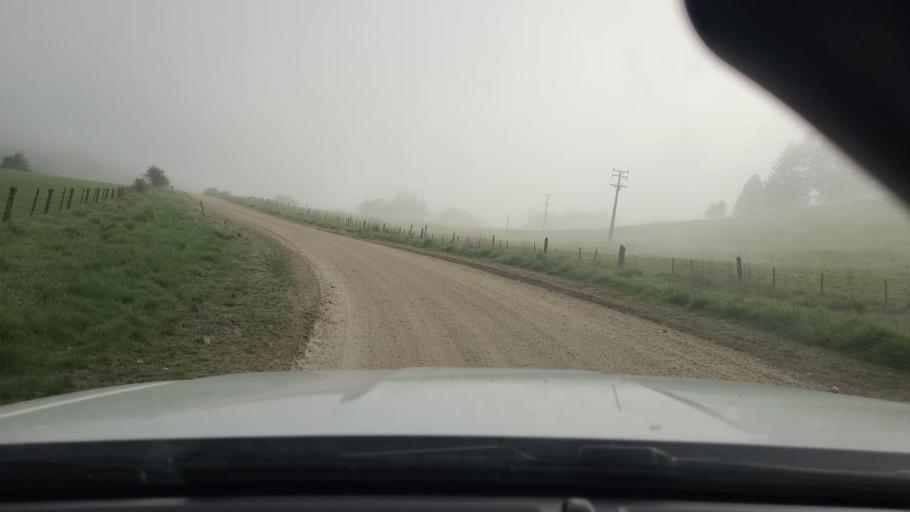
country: NZ
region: Otago
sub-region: Queenstown-Lakes District
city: Kingston
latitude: -45.5965
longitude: 168.9874
